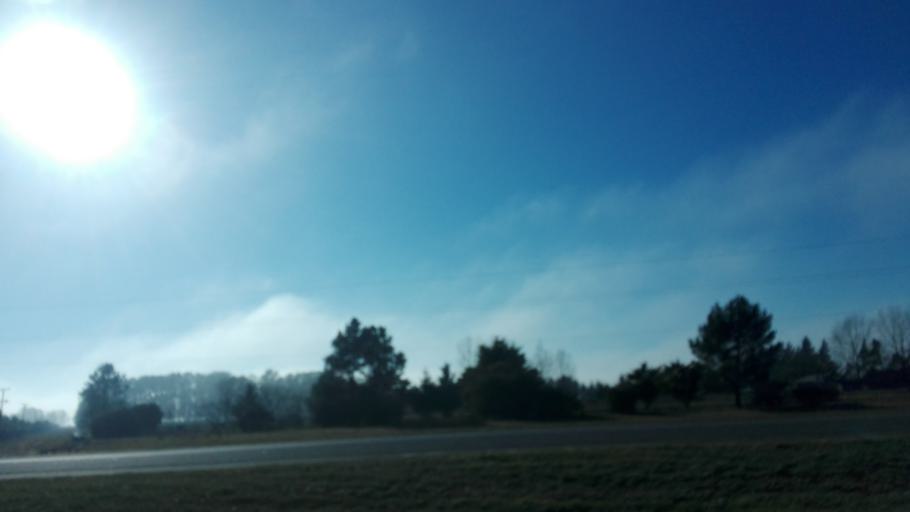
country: AR
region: Buenos Aires
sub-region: Partido de Chascomus
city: Chascomus
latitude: -35.4830
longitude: -58.0354
